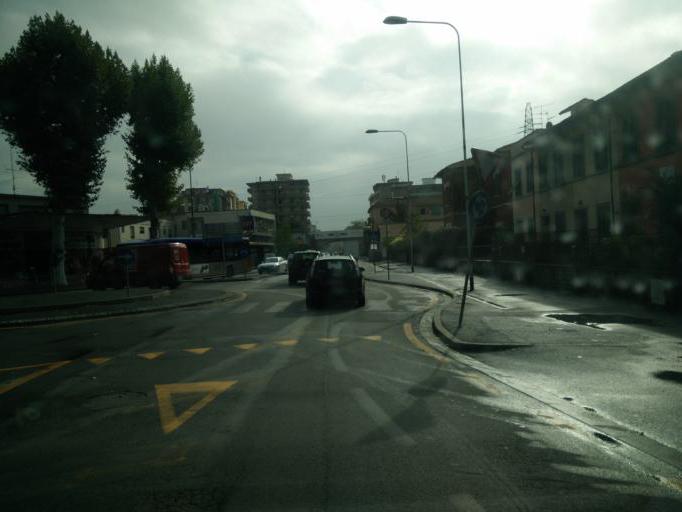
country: IT
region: Tuscany
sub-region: Province of Florence
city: Sesto Fiorentino
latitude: 43.7955
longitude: 11.2058
